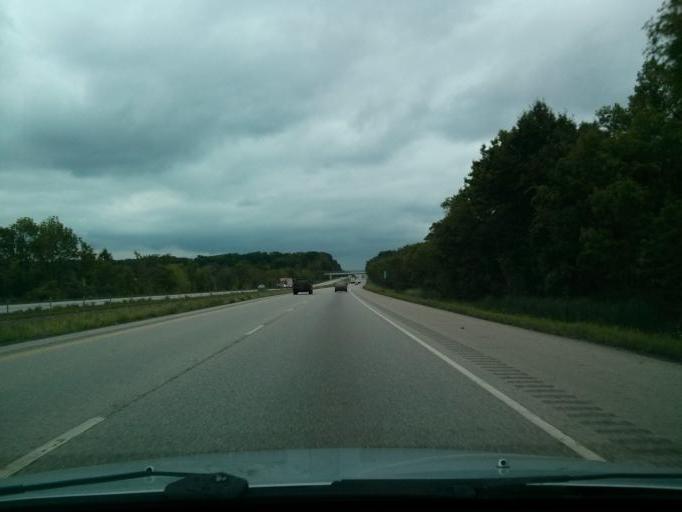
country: US
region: Ohio
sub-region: Mahoning County
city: Craig Beach
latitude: 41.1058
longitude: -81.0969
